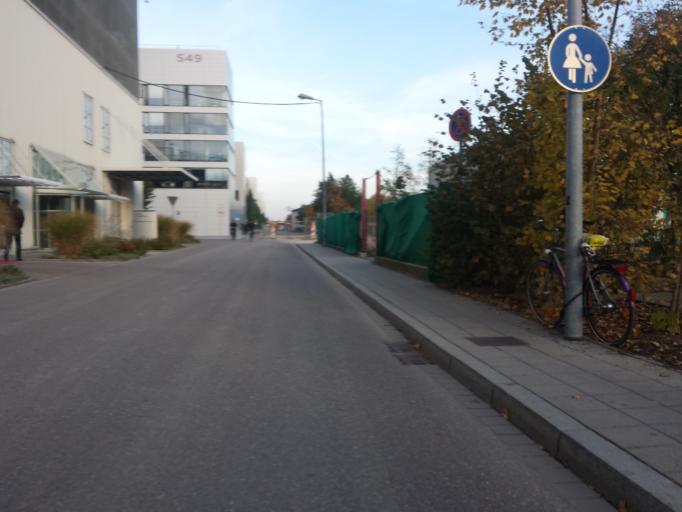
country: DE
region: Bavaria
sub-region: Upper Bavaria
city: Ingolstadt
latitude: 48.7815
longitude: 11.4170
